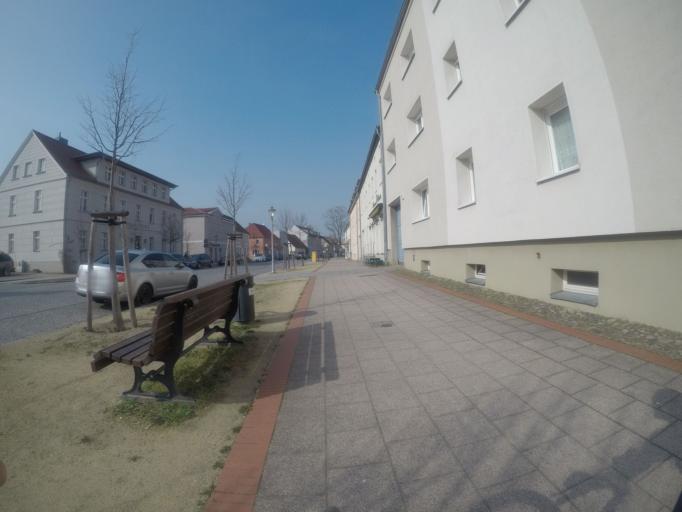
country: DE
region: Brandenburg
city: Mittenwalde
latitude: 52.2639
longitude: 13.5364
